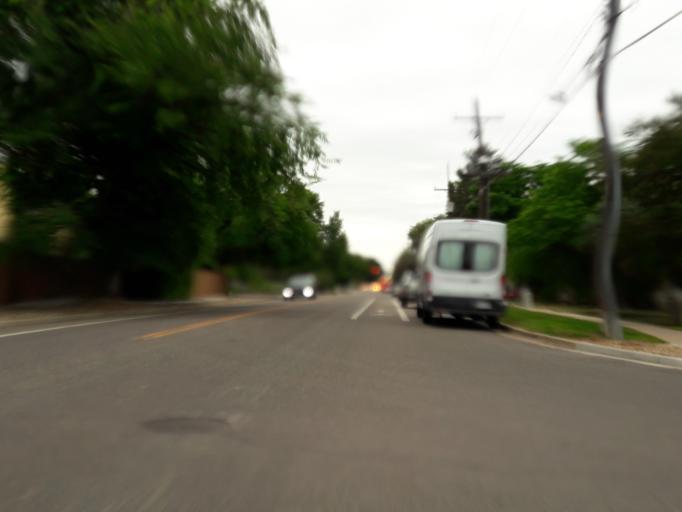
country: US
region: Colorado
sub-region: Boulder County
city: Boulder
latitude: 40.0401
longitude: -105.2612
